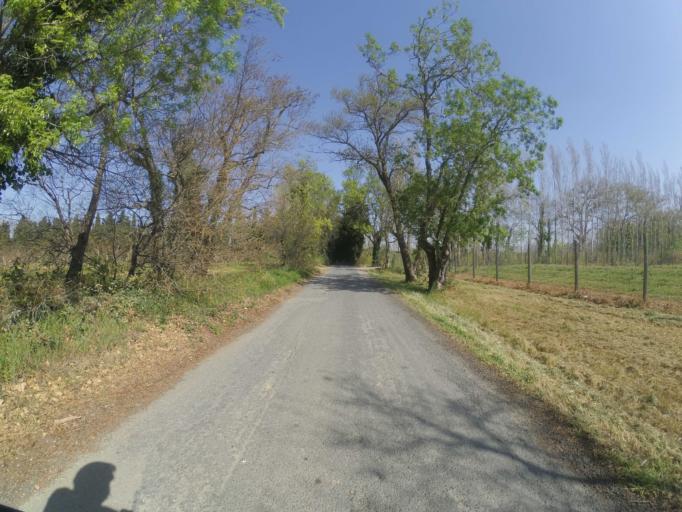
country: FR
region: Languedoc-Roussillon
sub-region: Departement des Pyrenees-Orientales
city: Pezilla-la-Riviere
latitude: 42.6651
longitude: 2.7593
